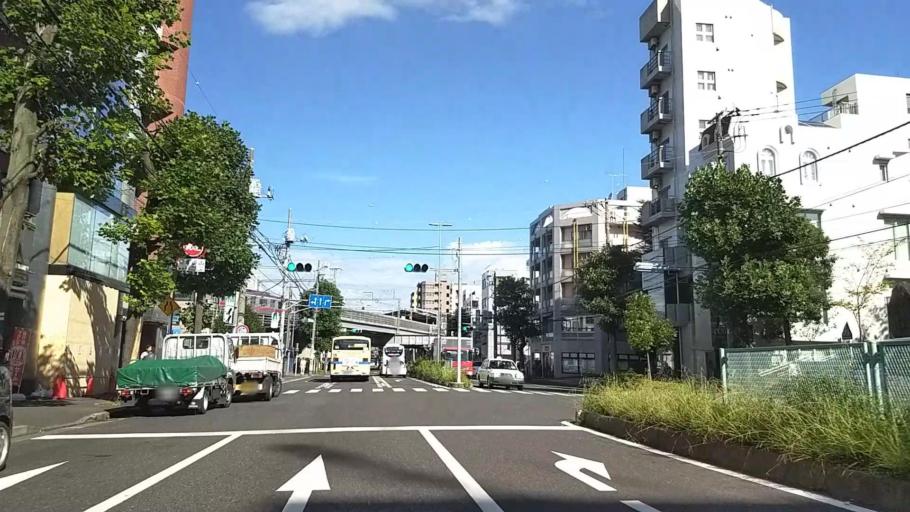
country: JP
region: Kanagawa
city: Yokohama
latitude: 35.4817
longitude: 139.6306
